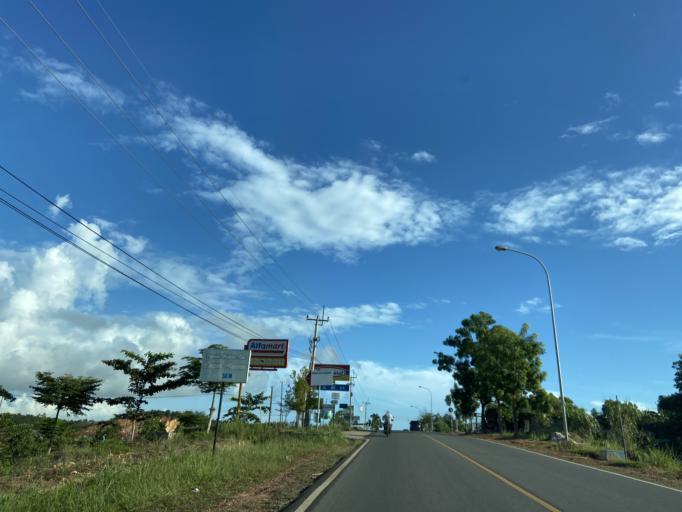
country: SG
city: Singapore
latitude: 1.0085
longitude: 104.0223
